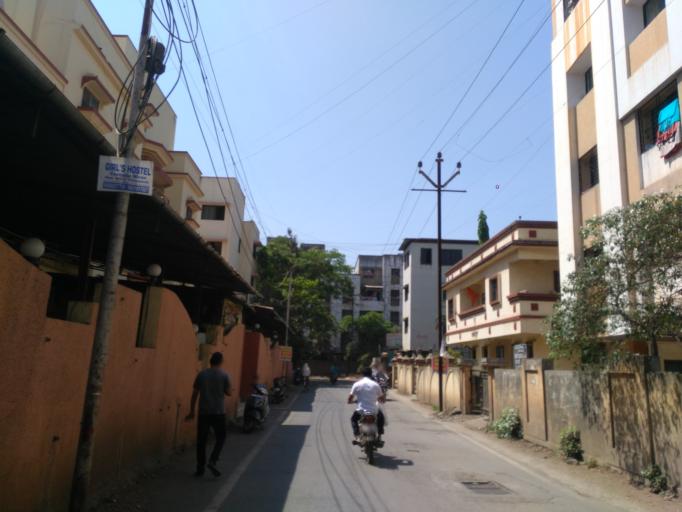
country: IN
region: Maharashtra
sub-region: Pune Division
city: Pune
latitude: 18.4534
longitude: 73.8534
